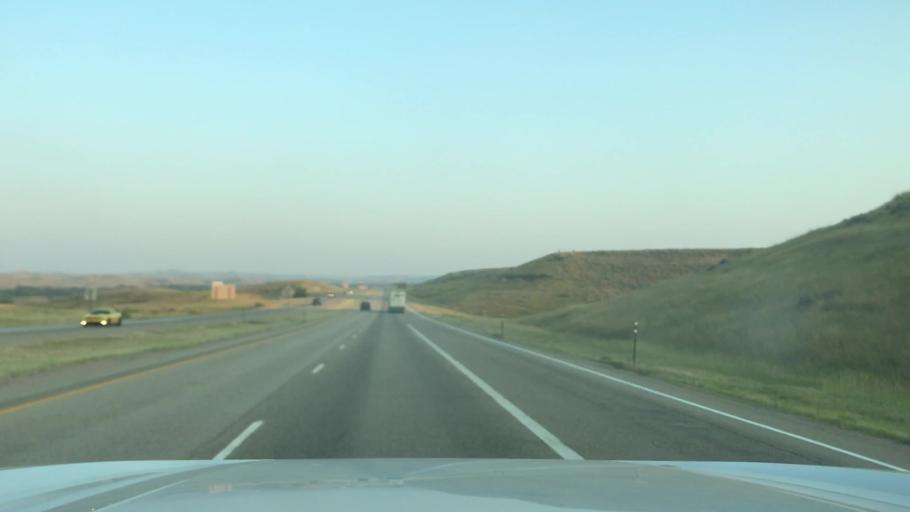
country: US
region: Wyoming
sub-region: Sheridan County
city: Sheridan
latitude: 44.8803
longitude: -107.0020
